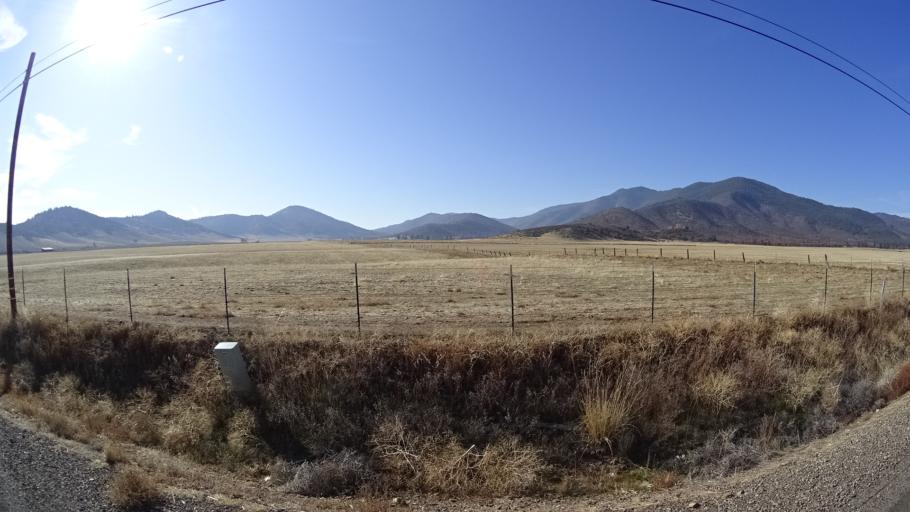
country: US
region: California
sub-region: Siskiyou County
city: Montague
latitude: 41.6538
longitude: -122.5642
